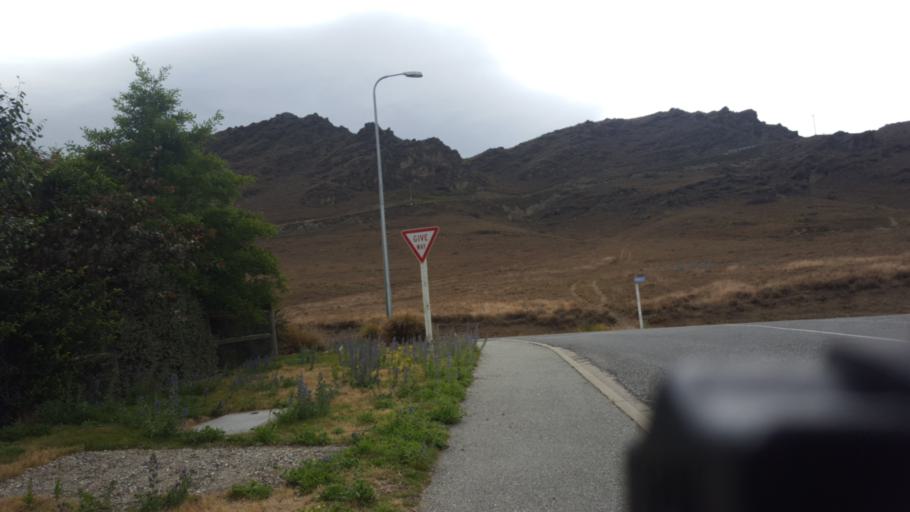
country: NZ
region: Otago
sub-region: Queenstown-Lakes District
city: Wanaka
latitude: -45.2520
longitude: 169.4044
